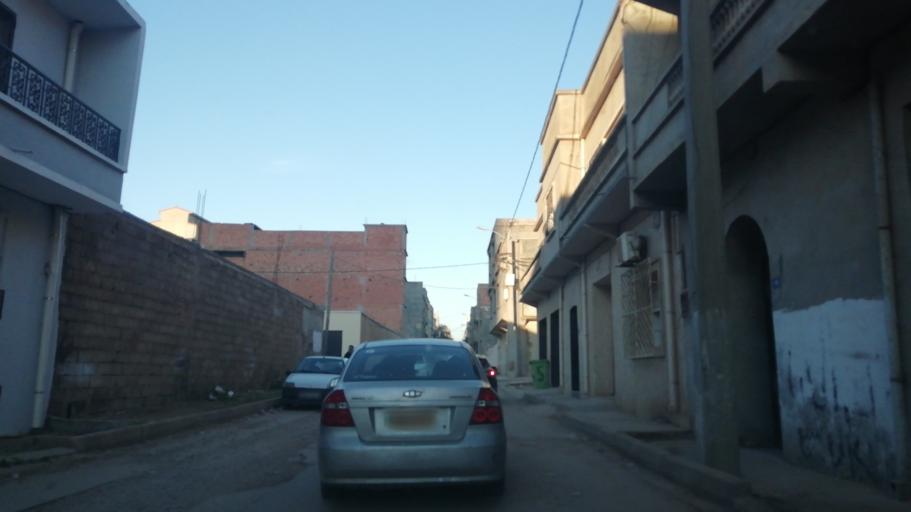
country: DZ
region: Oran
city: Bir el Djir
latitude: 35.7291
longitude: -0.5844
